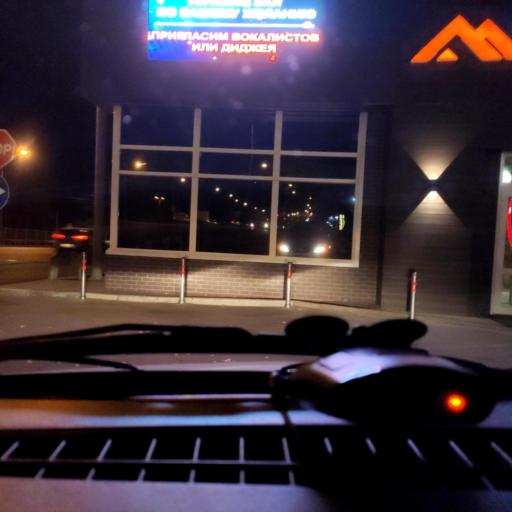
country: RU
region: Voronezj
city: Pridonskoy
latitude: 51.6474
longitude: 39.1126
